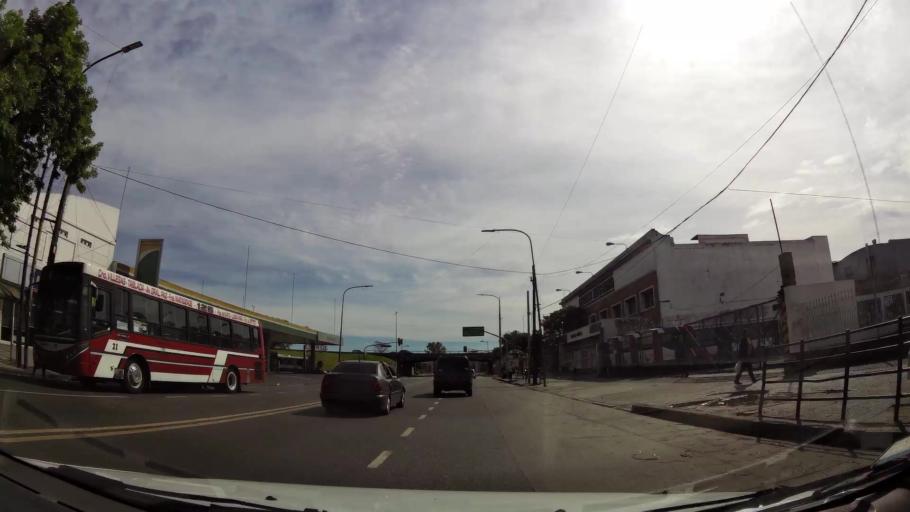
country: AR
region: Buenos Aires F.D.
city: Villa Lugano
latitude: -34.6736
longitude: -58.5011
